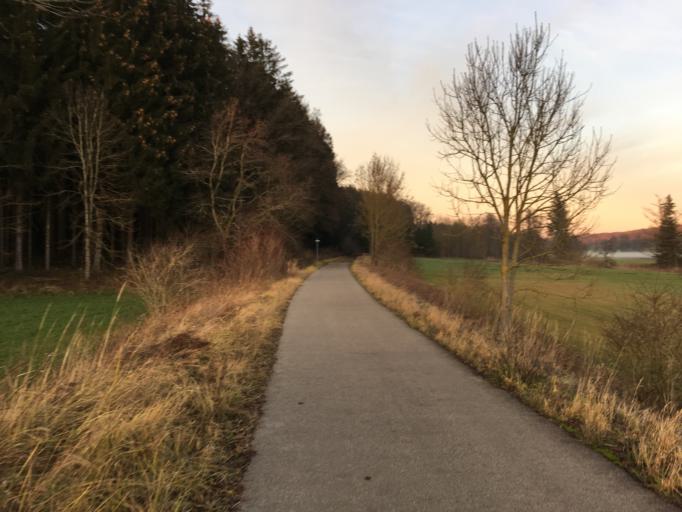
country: DE
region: Bavaria
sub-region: Swabia
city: Wald
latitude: 47.9764
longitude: 10.2826
